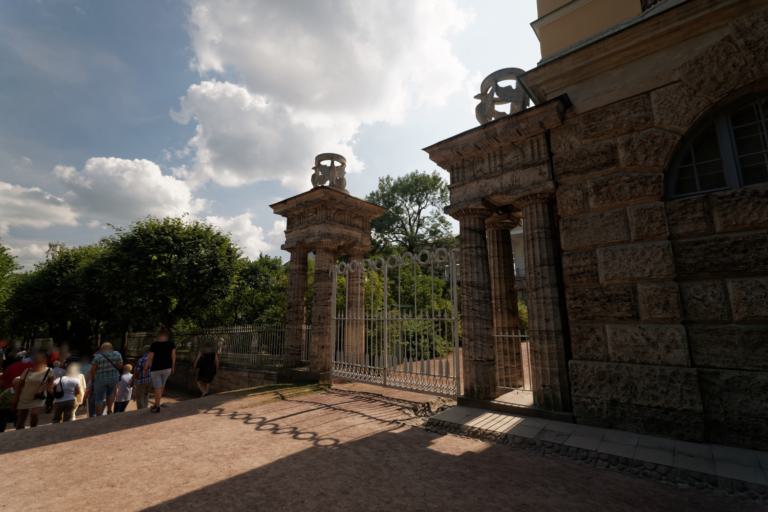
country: RU
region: St.-Petersburg
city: Pushkin
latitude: 59.7151
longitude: 30.3955
